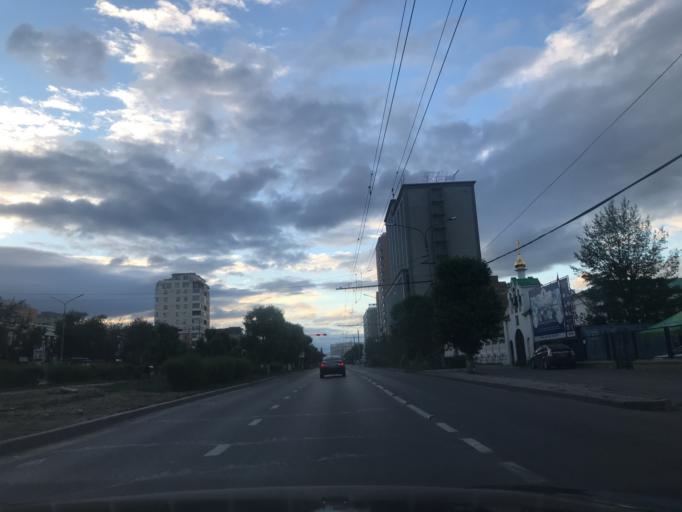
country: MN
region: Ulaanbaatar
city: Ulaanbaatar
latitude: 47.9169
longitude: 106.9585
